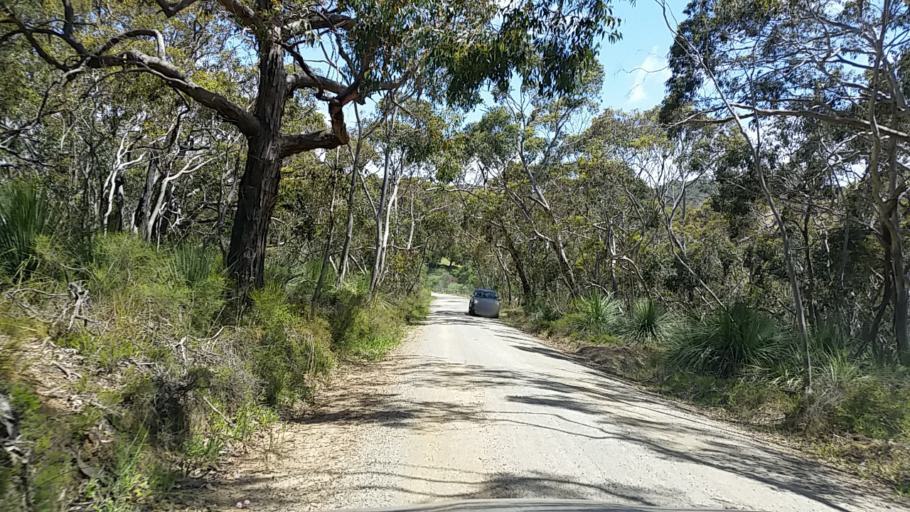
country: AU
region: South Australia
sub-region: Alexandrina
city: Mount Compass
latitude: -35.4391
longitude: 138.5831
